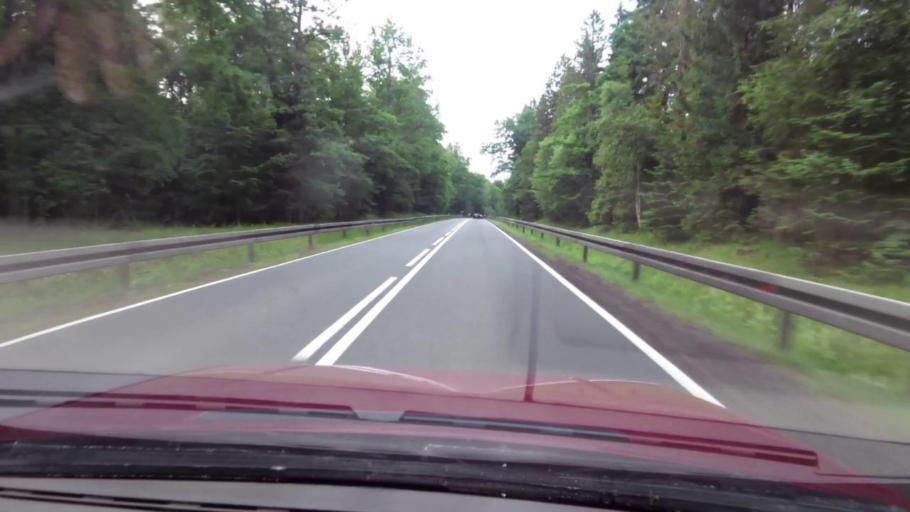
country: PL
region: Pomeranian Voivodeship
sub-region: Powiat bytowski
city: Trzebielino
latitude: 54.2288
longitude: 17.0867
